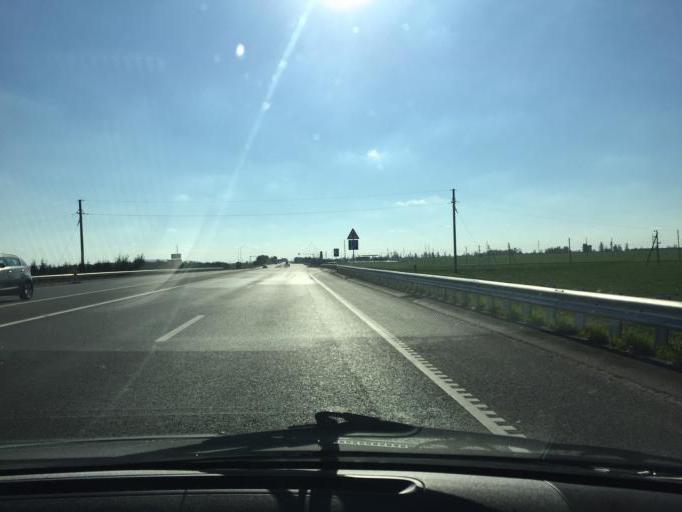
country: BY
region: Minsk
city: Slutsk
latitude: 52.9899
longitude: 27.5070
